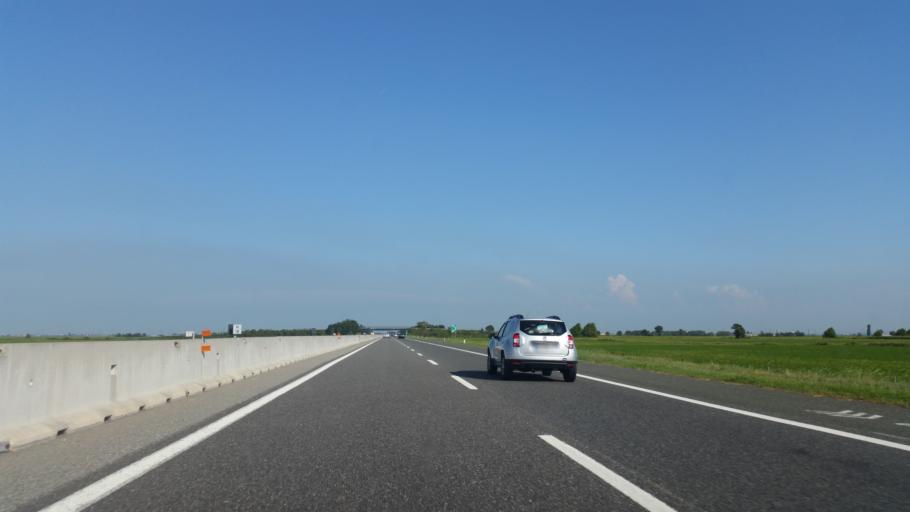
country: IT
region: Piedmont
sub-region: Provincia di Vercelli
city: Salasco
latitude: 45.3190
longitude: 8.2604
